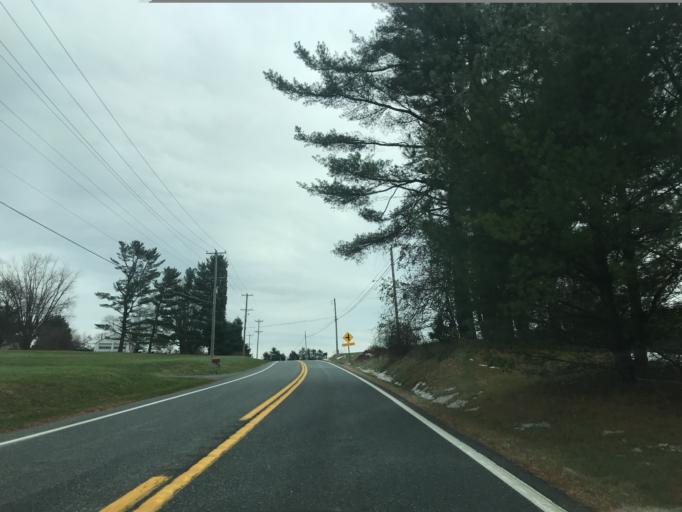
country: US
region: Pennsylvania
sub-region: York County
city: Susquehanna Trails
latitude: 39.6677
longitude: -76.3518
